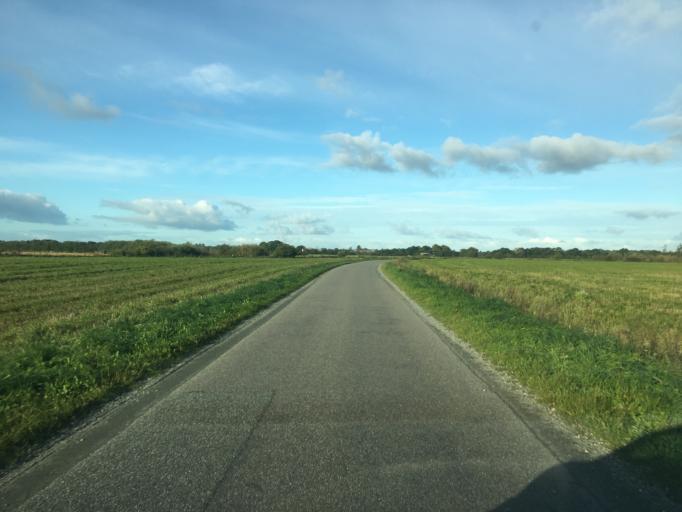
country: DK
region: South Denmark
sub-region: Tonder Kommune
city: Logumkloster
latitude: 55.0737
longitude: 8.9691
